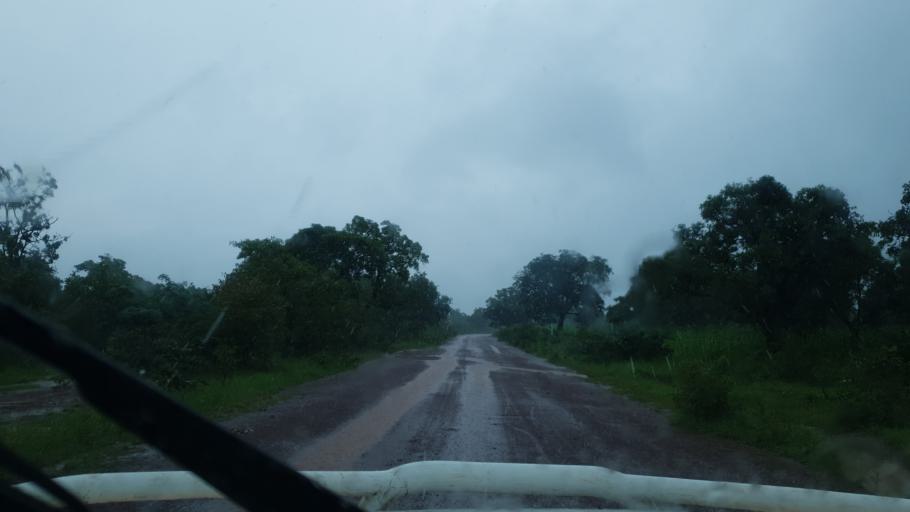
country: ML
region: Sikasso
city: Kolondieba
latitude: 11.6106
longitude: -6.6757
